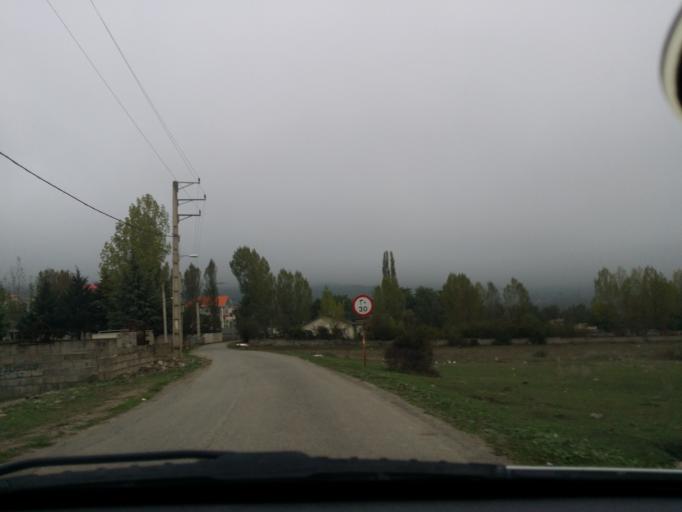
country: IR
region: Mazandaran
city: Chalus
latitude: 36.5138
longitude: 51.2260
